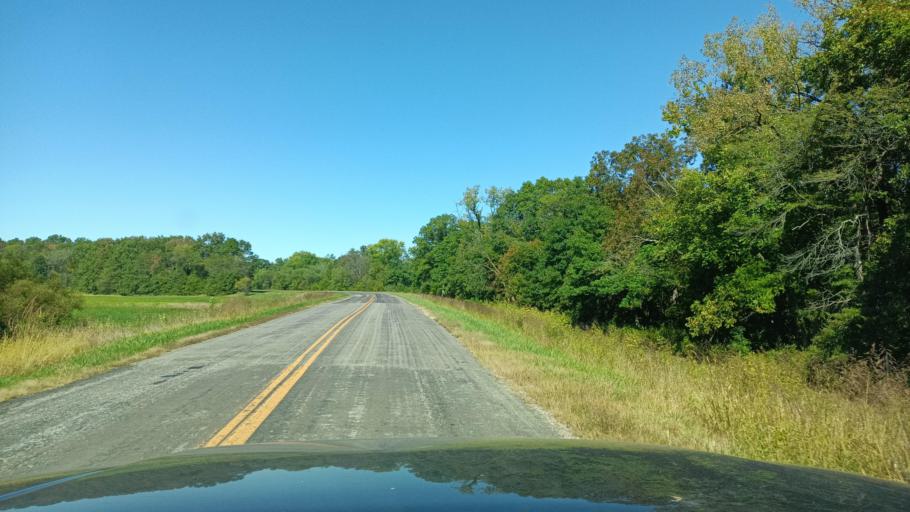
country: US
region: Missouri
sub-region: Scotland County
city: Memphis
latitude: 40.3535
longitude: -92.2462
